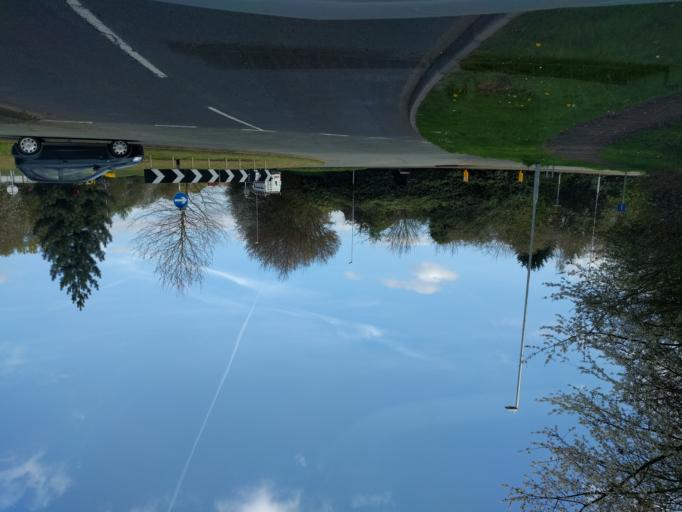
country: GB
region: England
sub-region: Northamptonshire
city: Earls Barton
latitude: 52.2574
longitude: -0.8099
